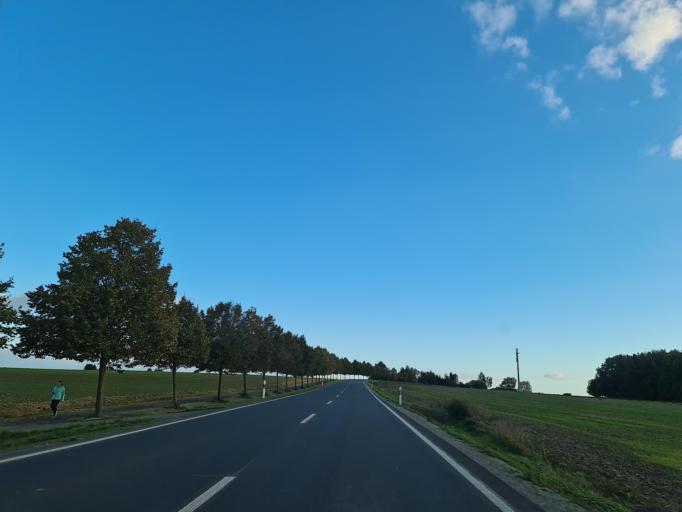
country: DE
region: Thuringia
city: Wildetaube
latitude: 50.7253
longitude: 12.1078
